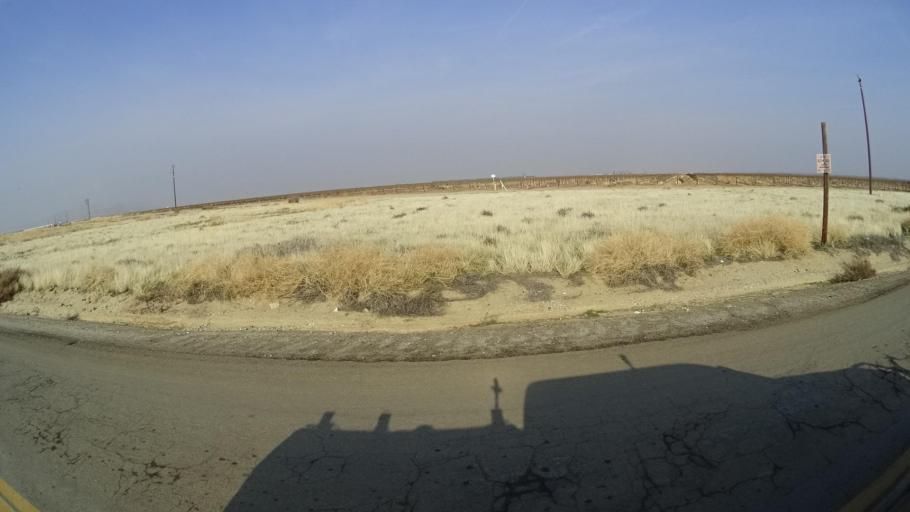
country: US
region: California
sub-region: Kern County
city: Lebec
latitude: 34.9930
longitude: -118.9065
